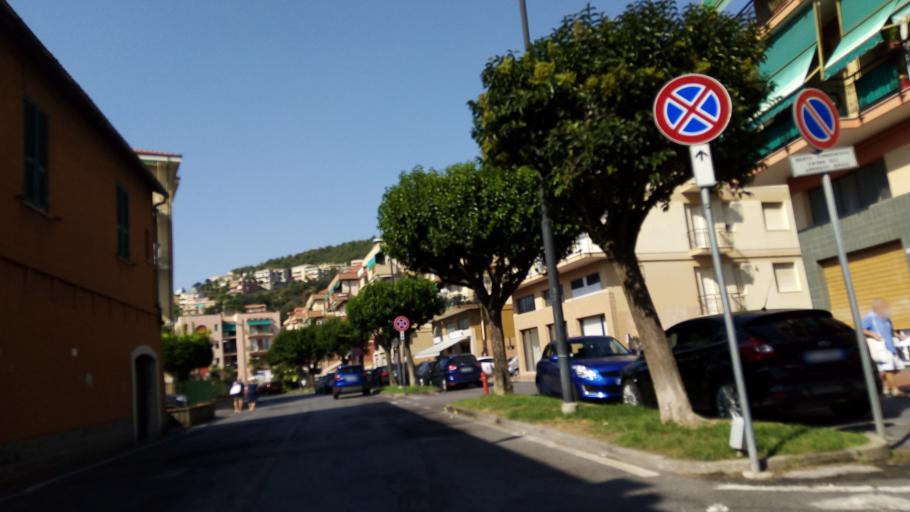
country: IT
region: Liguria
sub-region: Provincia di Savona
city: Pietra Ligure
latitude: 44.1549
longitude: 8.2877
